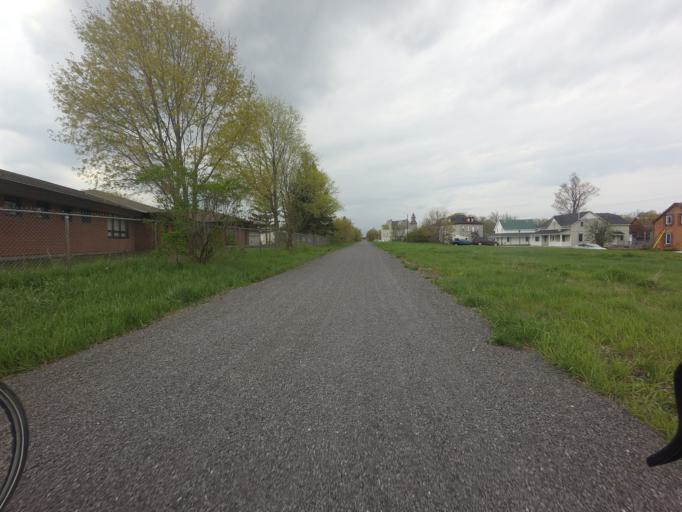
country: CA
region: Ontario
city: Carleton Place
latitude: 45.2243
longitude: -76.1924
